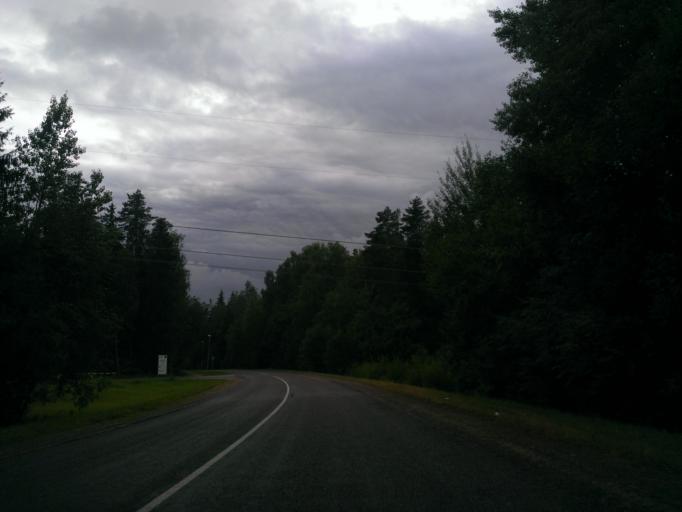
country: LV
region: Kegums
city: Kegums
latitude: 56.7545
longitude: 24.7358
